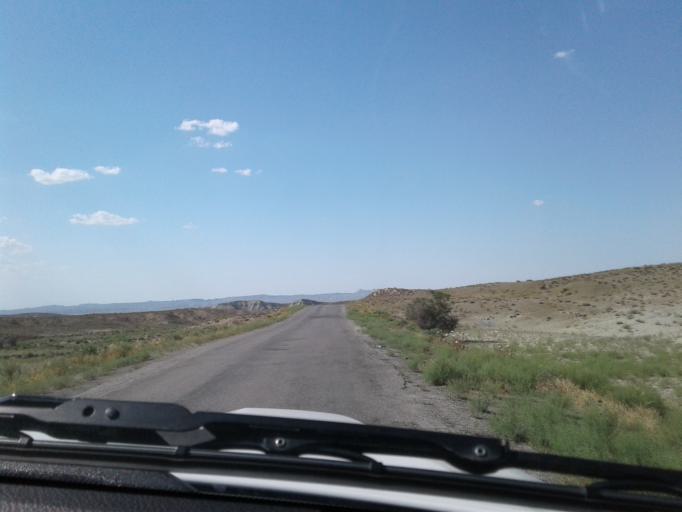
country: TM
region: Balkan
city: Magtymguly
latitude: 38.5096
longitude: 56.1908
